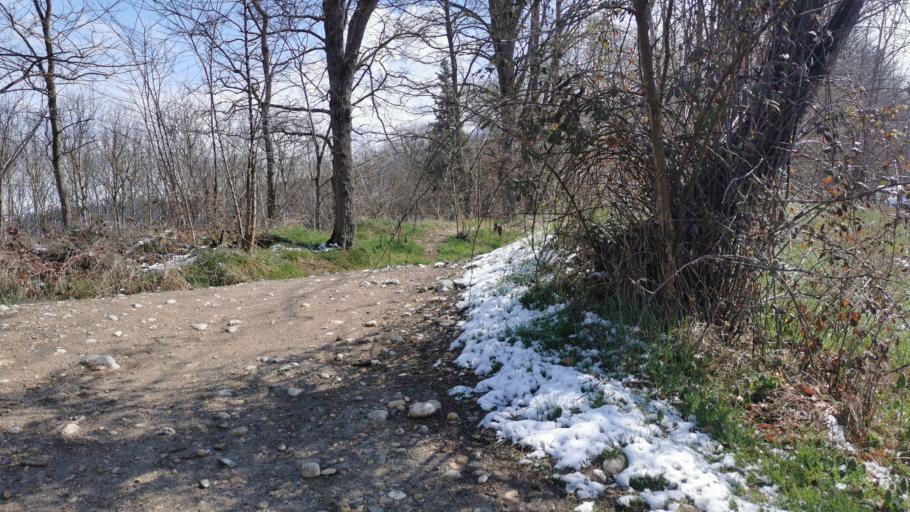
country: FR
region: Provence-Alpes-Cote d'Azur
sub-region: Departement des Alpes-de-Haute-Provence
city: Mallemoisson
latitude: 44.0568
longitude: 6.1699
